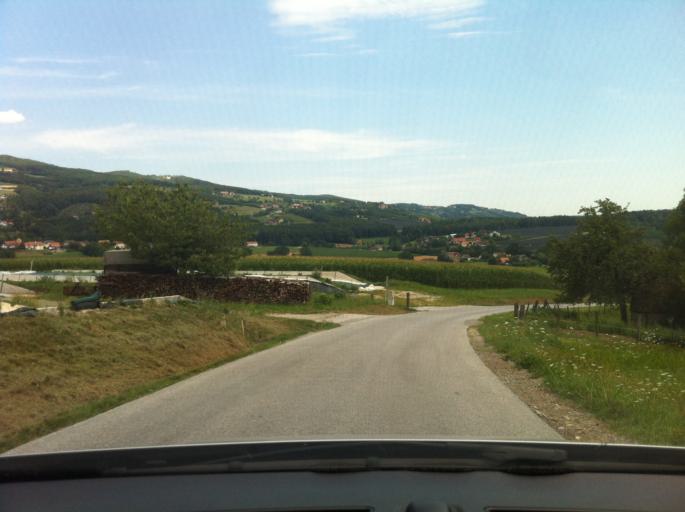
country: AT
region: Styria
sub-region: Politischer Bezirk Hartberg-Fuerstenfeld
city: Stubenberg
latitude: 47.2369
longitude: 15.7905
